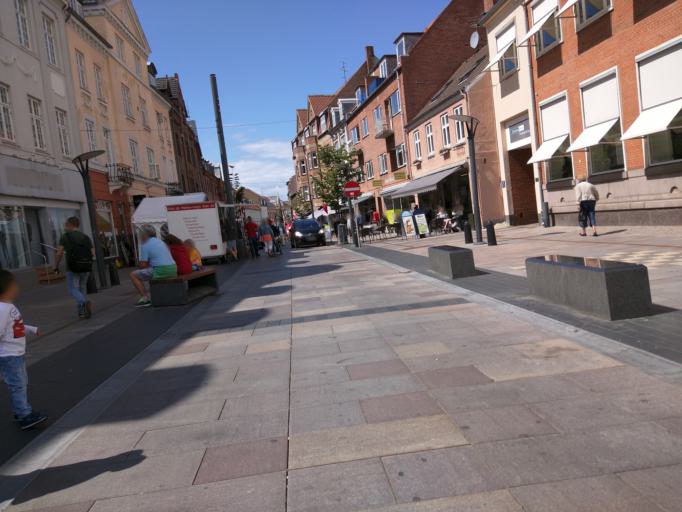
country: DK
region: Zealand
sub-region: Kalundborg Kommune
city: Kalundborg
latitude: 55.6798
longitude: 11.0930
